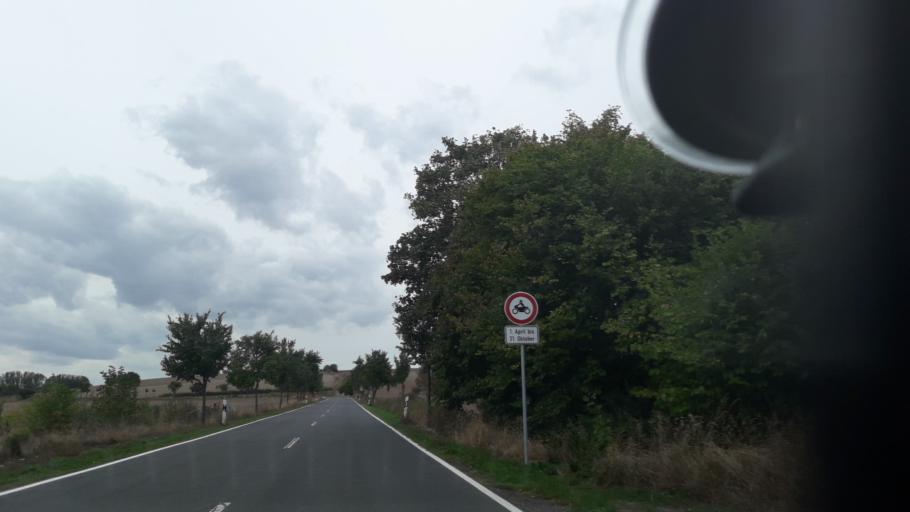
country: DE
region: Lower Saxony
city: Werlaburgdorf
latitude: 52.0508
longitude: 10.5287
